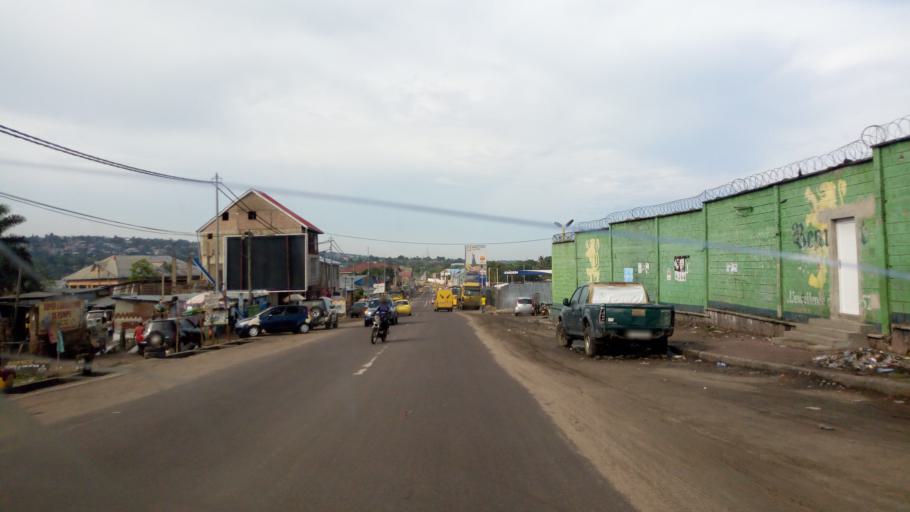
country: CD
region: Kinshasa
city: Kinshasa
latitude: -4.4414
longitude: 15.2561
